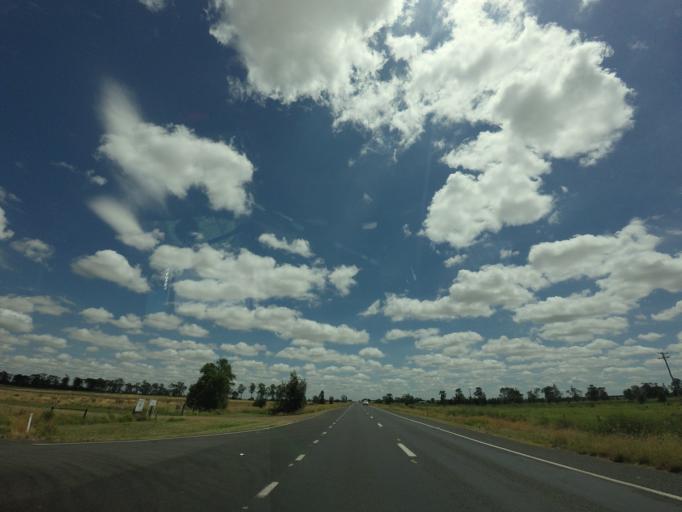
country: AU
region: New South Wales
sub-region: Moree Plains
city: Moree
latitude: -29.1637
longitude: 150.0139
